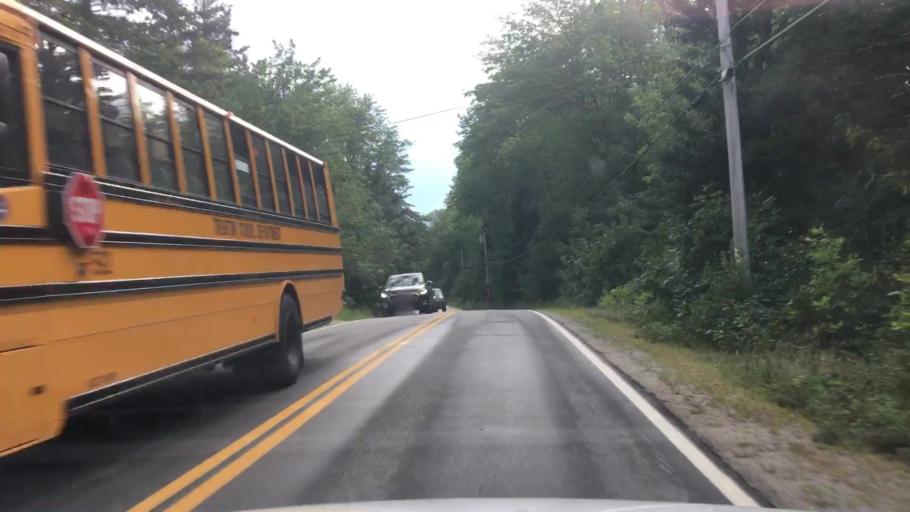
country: US
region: Maine
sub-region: Hancock County
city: Trenton
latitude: 44.4593
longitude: -68.4248
